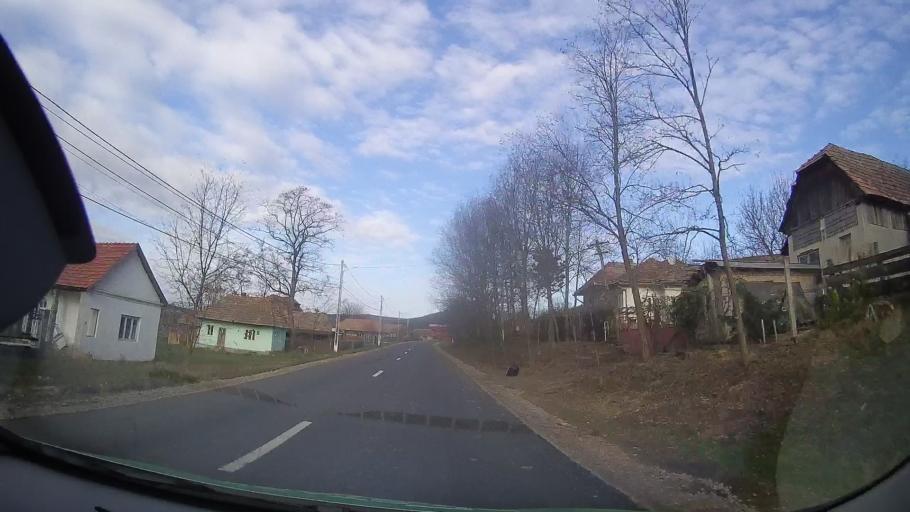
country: RO
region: Mures
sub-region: Comuna Iclanzel
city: Iclanzel
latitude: 46.5193
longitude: 24.2735
